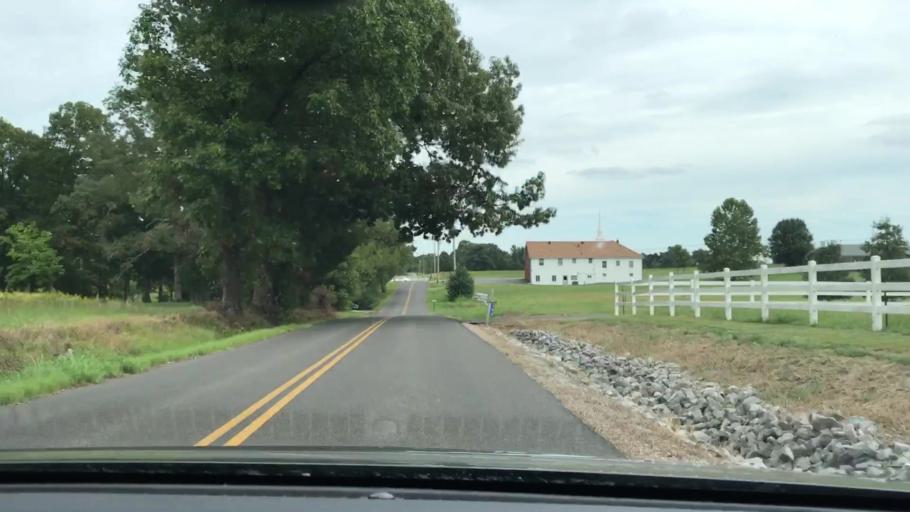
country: US
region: Kentucky
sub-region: Marshall County
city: Benton
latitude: 36.8311
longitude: -88.3529
